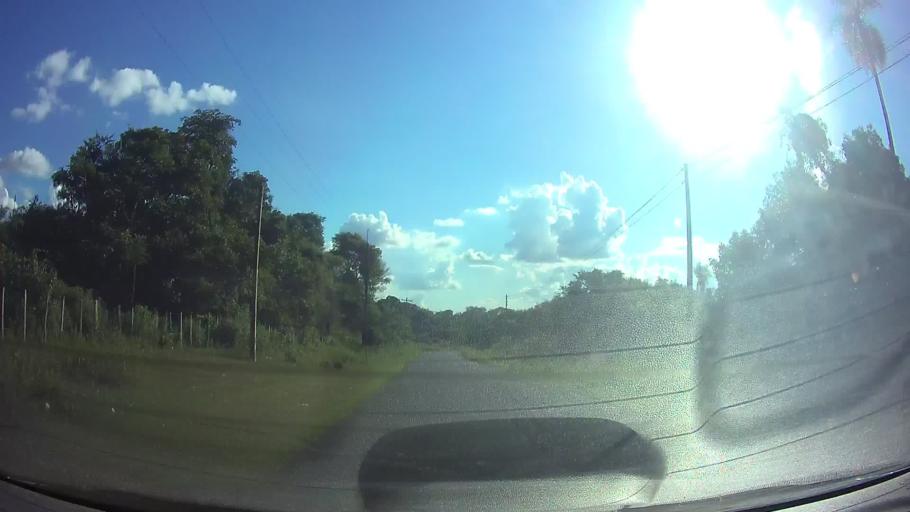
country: PY
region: Central
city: Aregua
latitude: -25.3331
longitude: -57.3787
